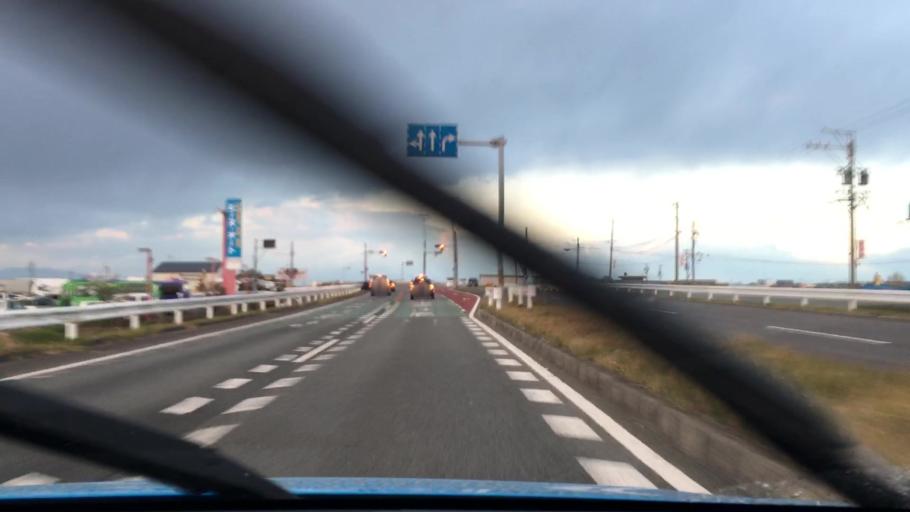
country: JP
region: Mie
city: Ise
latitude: 34.5482
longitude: 136.6586
